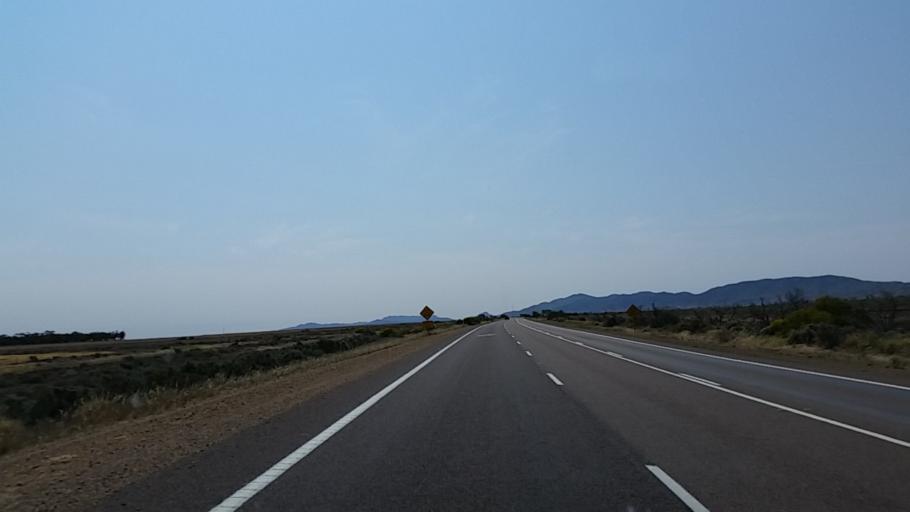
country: AU
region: South Australia
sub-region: Port Augusta
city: Port Augusta
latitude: -32.7136
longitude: 137.9404
